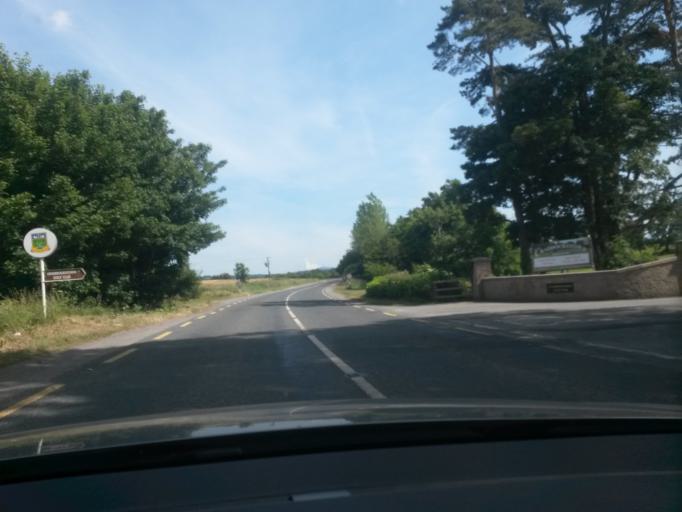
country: IE
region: Leinster
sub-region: Kildare
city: Naas
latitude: 53.2090
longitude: -6.6399
